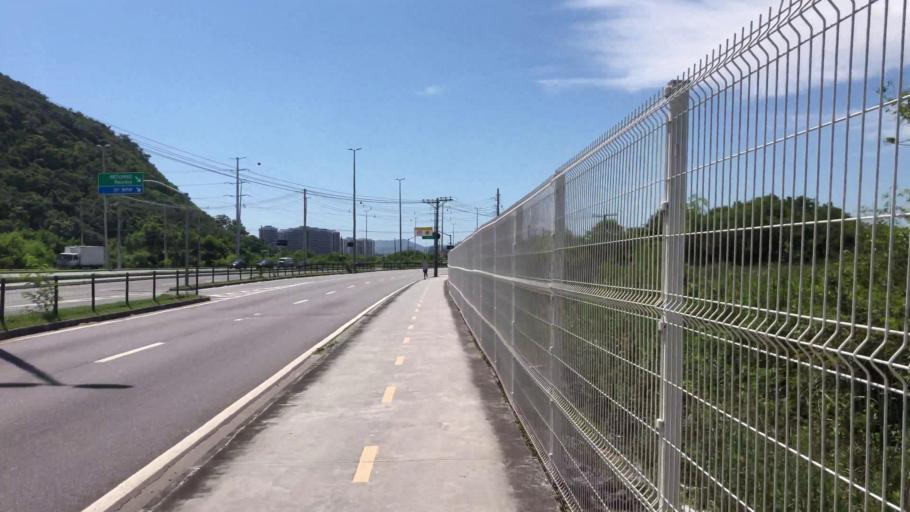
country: BR
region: Rio de Janeiro
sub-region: Nilopolis
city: Nilopolis
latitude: -22.9735
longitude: -43.3893
